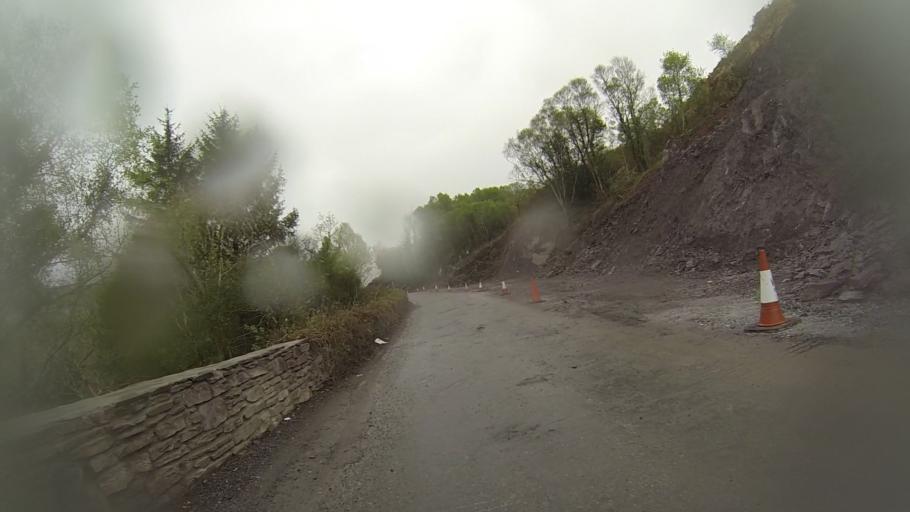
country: IE
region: Munster
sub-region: Ciarrai
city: Kenmare
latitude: 51.8057
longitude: -9.5569
